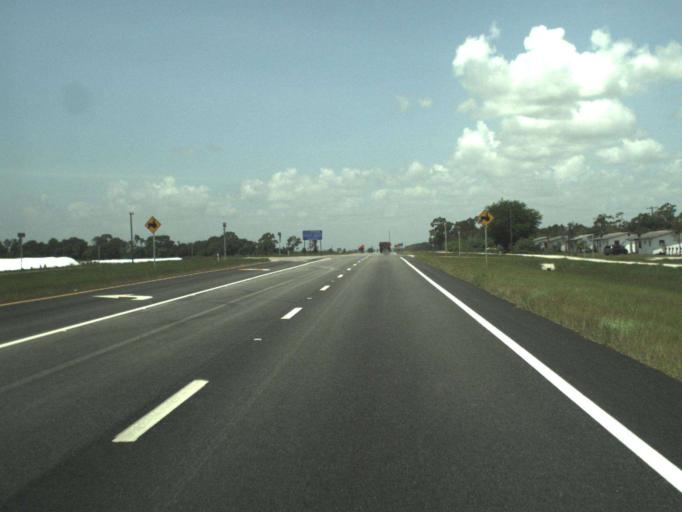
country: US
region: Florida
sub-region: Okeechobee County
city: Taylor Creek
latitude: 27.3042
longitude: -80.6740
